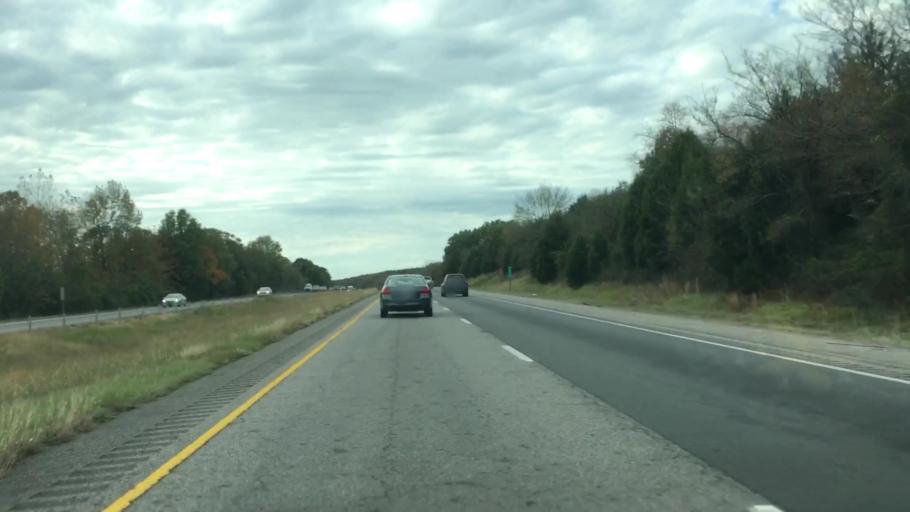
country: US
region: Arkansas
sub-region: Faulkner County
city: Conway
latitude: 35.1556
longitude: -92.5613
